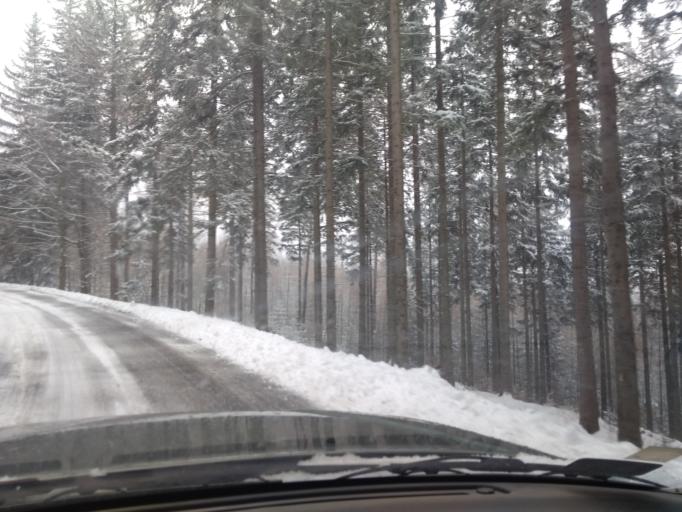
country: PL
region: Lower Silesian Voivodeship
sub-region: Powiat jeleniogorski
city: Sosnowka
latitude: 50.7895
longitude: 15.7163
